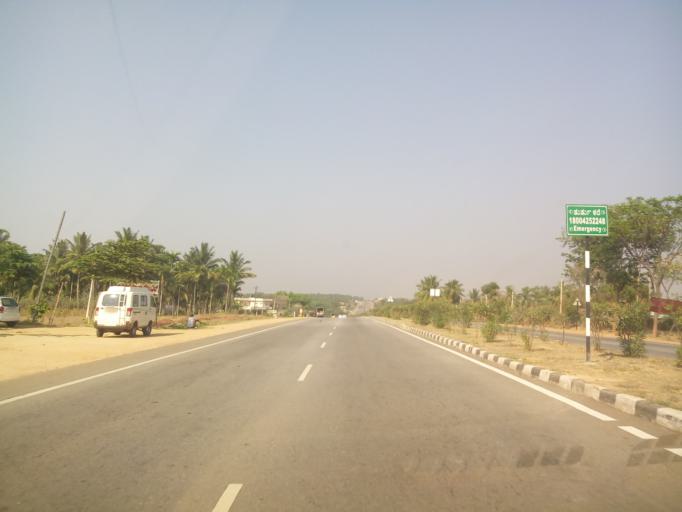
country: IN
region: Karnataka
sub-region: Tumkur
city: Kunigal
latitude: 13.0411
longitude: 77.1108
